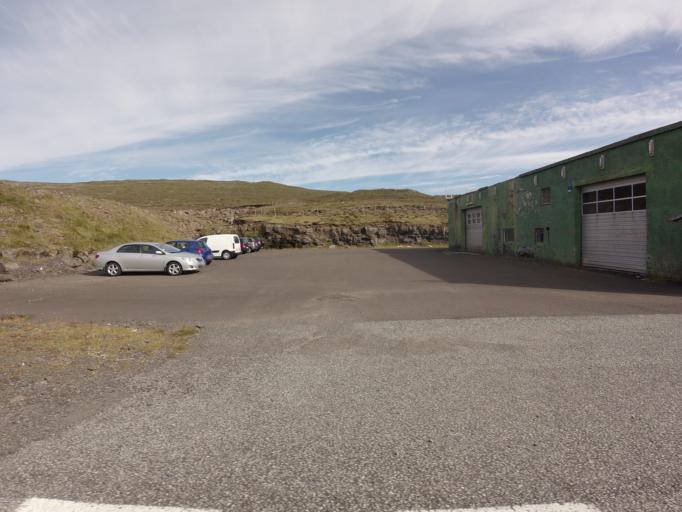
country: FO
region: Vagar
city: Sorvagur
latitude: 62.0699
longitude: -7.2790
